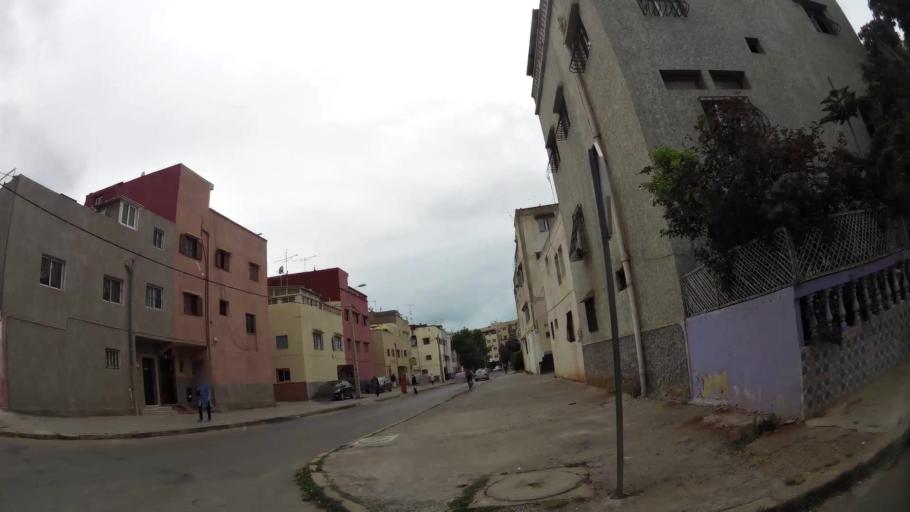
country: MA
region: Rabat-Sale-Zemmour-Zaer
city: Sale
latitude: 34.0483
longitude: -6.7988
